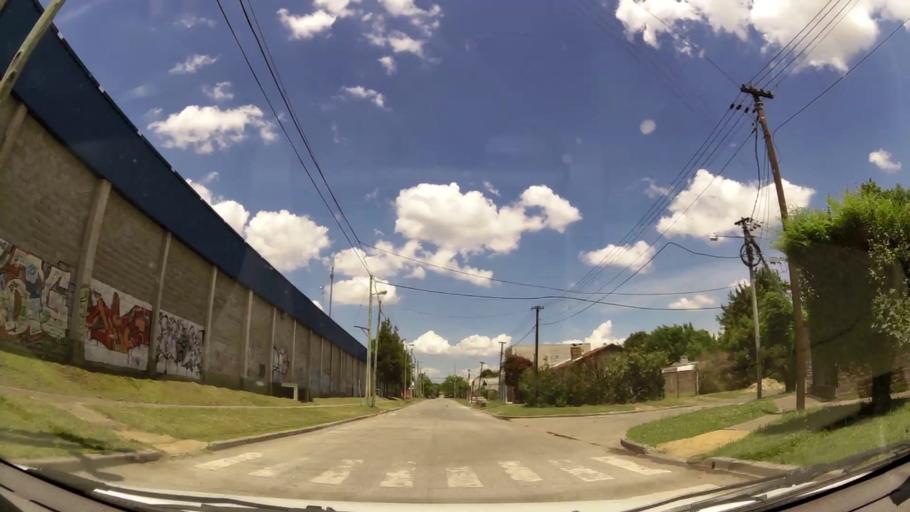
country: AR
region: Buenos Aires
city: Ituzaingo
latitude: -34.6479
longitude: -58.6890
